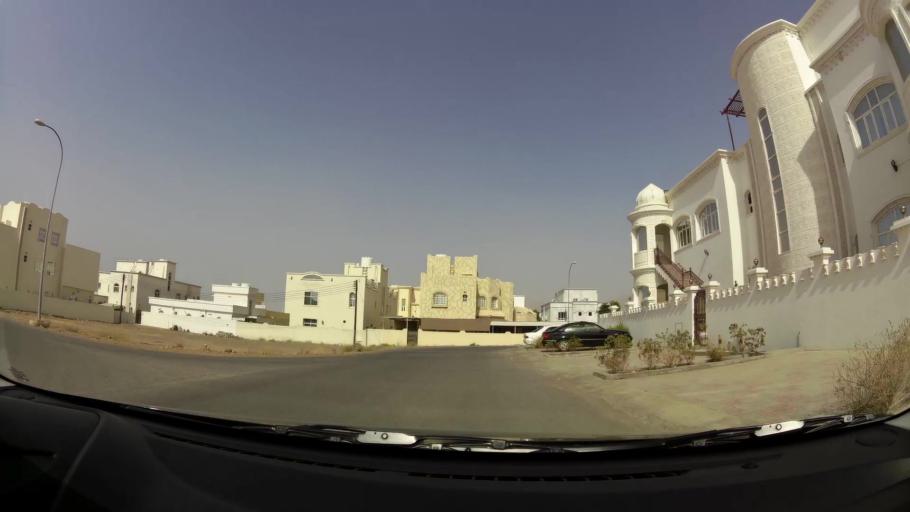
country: OM
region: Muhafazat Masqat
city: Bawshar
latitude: 23.5530
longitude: 58.3549
